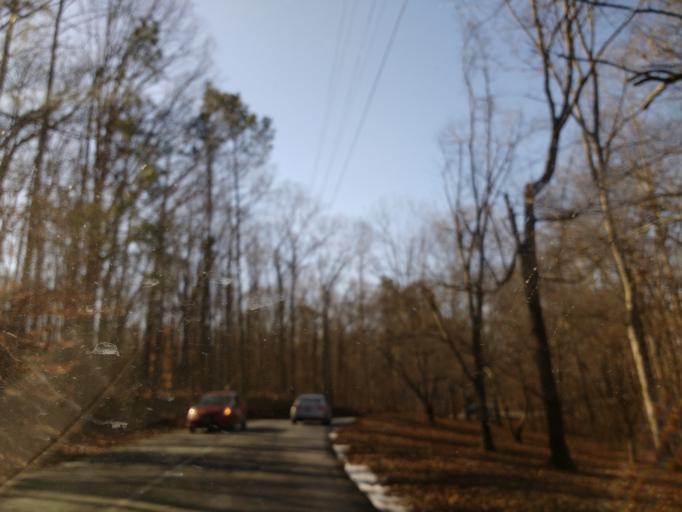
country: US
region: Georgia
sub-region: Douglas County
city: Lithia Springs
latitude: 33.7536
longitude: -84.6350
